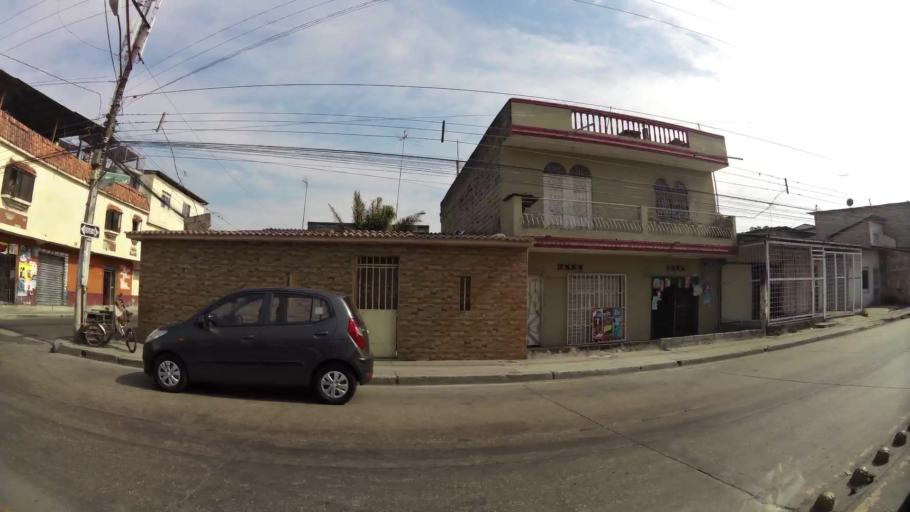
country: EC
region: Guayas
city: Guayaquil
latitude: -2.2556
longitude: -79.8996
